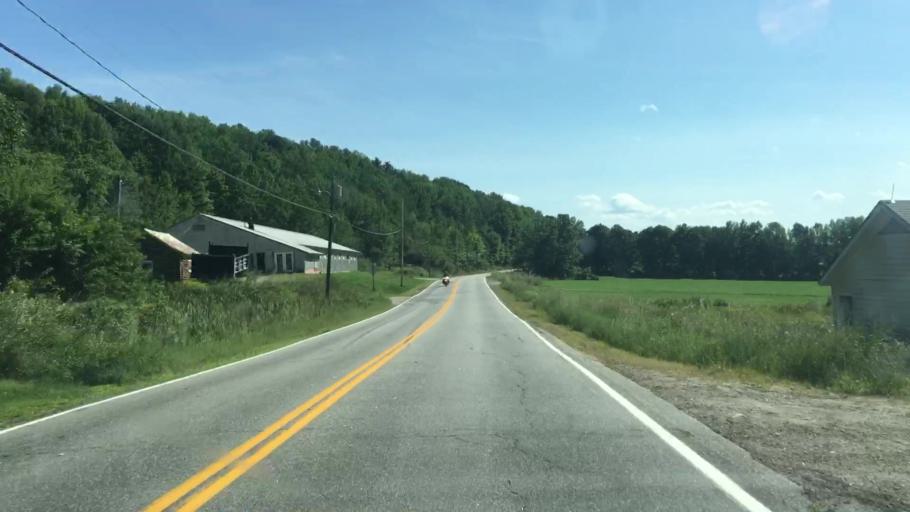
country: US
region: Maine
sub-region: Androscoggin County
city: Sabattus
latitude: 44.1383
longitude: -70.0874
